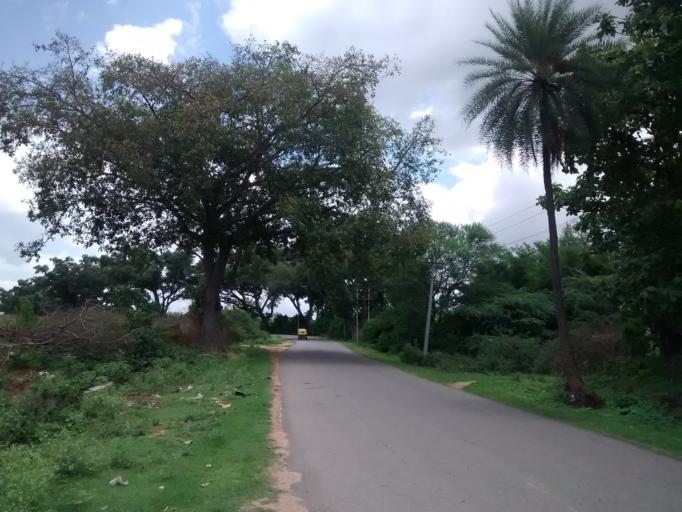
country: IN
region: Karnataka
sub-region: Tumkur
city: Kunigal
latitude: 13.1139
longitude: 77.1594
